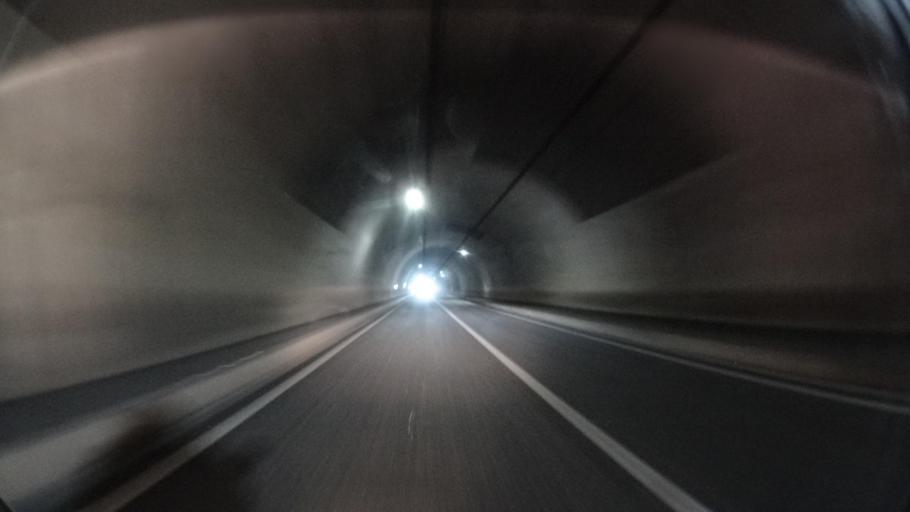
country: JP
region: Kyoto
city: Maizuru
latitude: 35.5245
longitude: 135.3455
